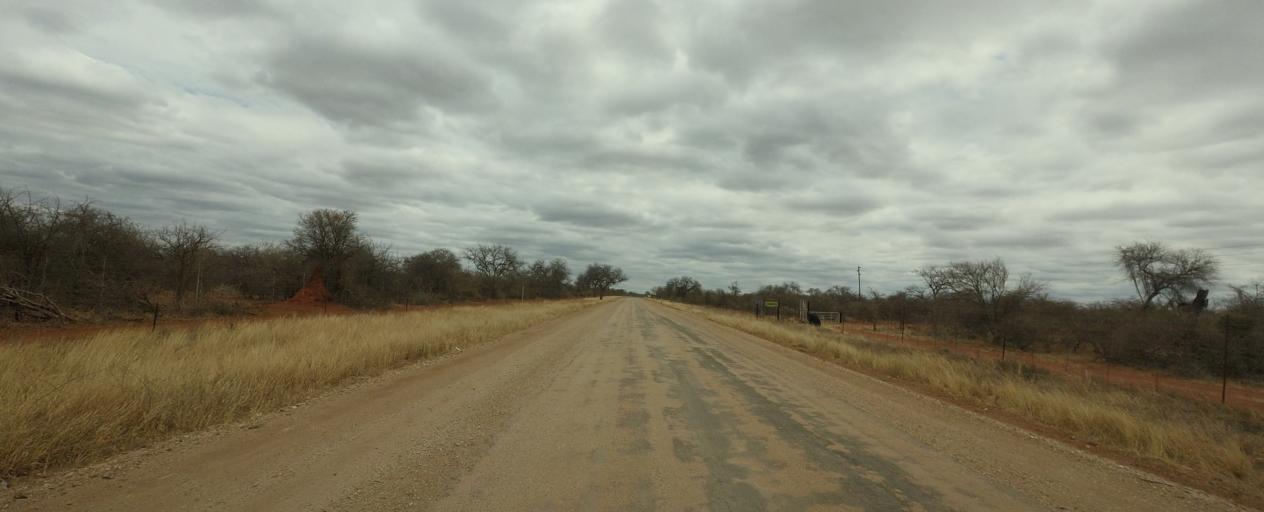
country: BW
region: Central
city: Mathathane
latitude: -22.7083
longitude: 28.5844
